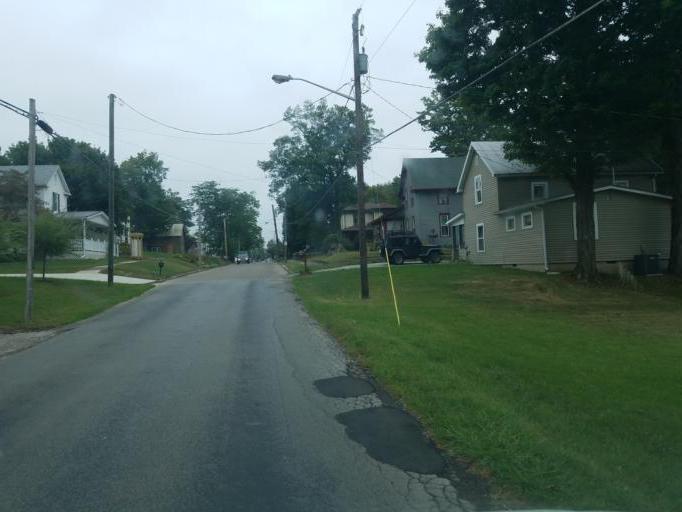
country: US
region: Ohio
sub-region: Knox County
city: Centerburg
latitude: 40.2994
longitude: -82.6931
